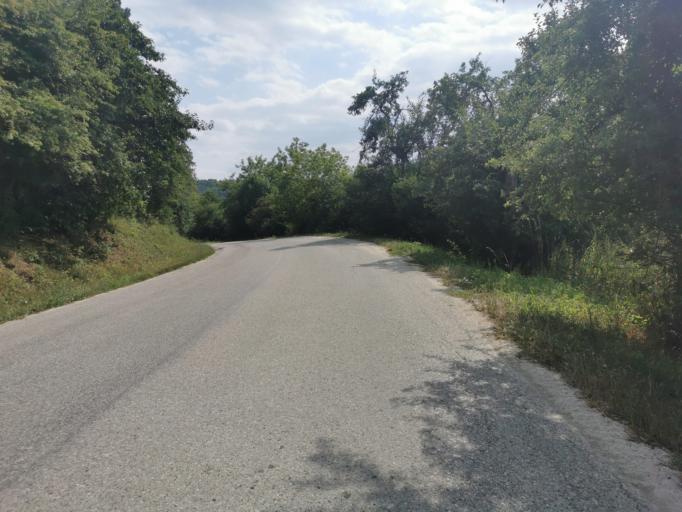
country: SK
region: Trenciansky
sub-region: Okres Myjava
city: Myjava
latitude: 48.7471
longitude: 17.5206
